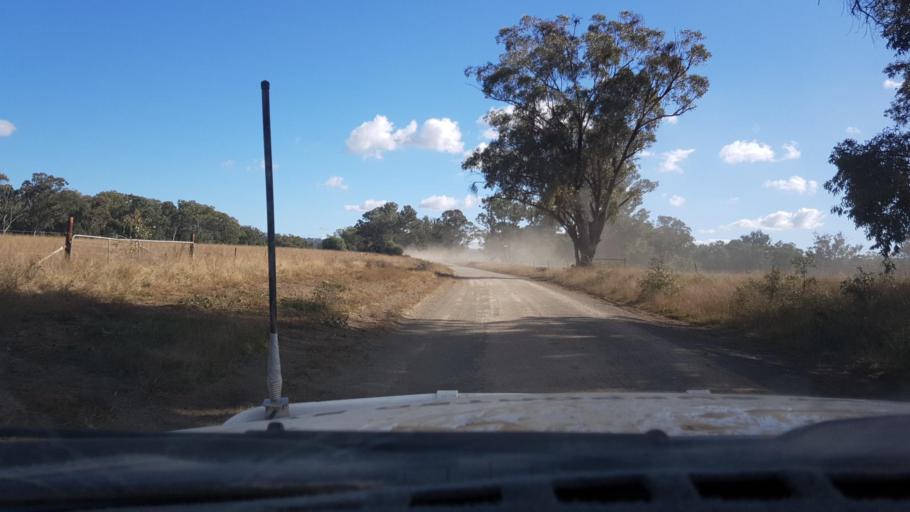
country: AU
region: New South Wales
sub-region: Tamworth Municipality
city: Manilla
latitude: -30.5927
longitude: 150.4931
